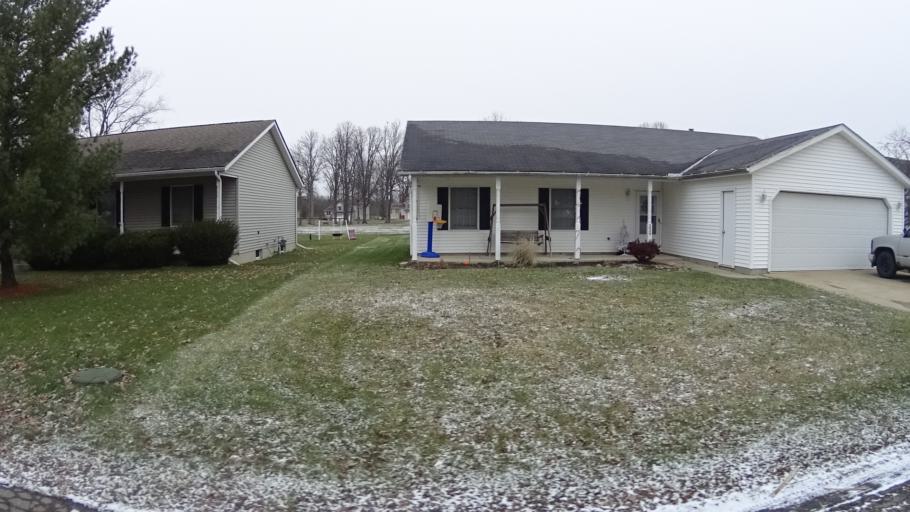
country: US
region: Ohio
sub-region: Lorain County
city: Lagrange
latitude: 41.2046
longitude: -82.1494
